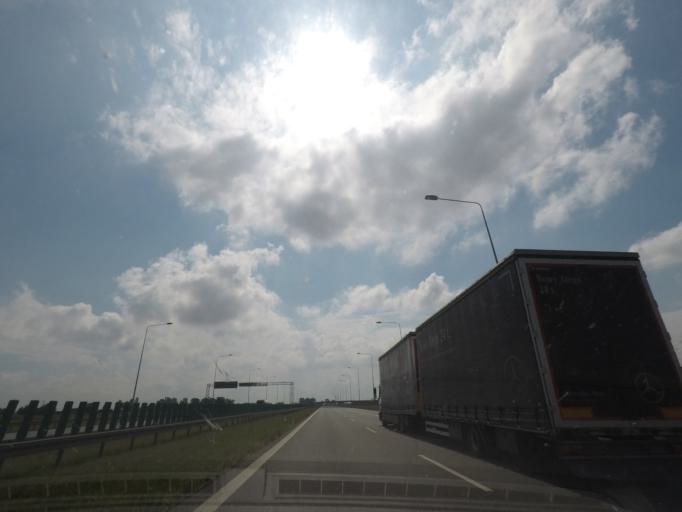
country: PL
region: Lodz Voivodeship
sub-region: Powiat kutnowski
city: Krzyzanow
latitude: 52.2246
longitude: 19.4657
